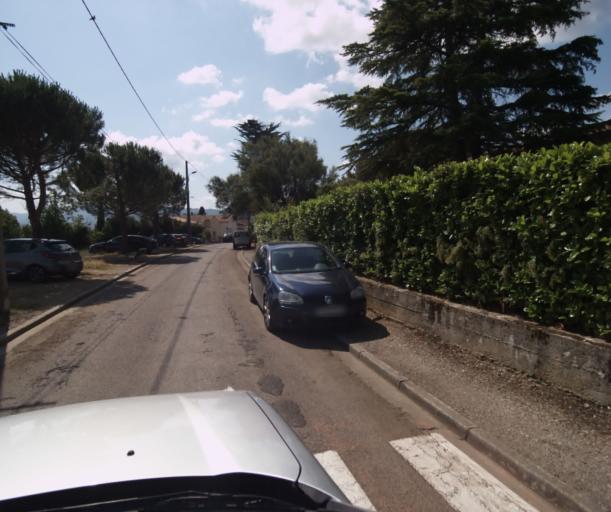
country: FR
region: Languedoc-Roussillon
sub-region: Departement de l'Aude
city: Limoux
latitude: 43.0531
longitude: 2.2128
